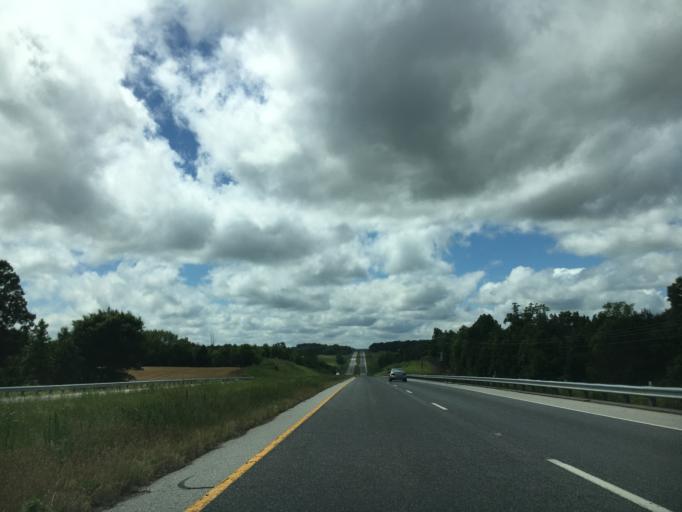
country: US
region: Virginia
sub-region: Mecklenburg County
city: Boydton
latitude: 36.6715
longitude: -78.2639
